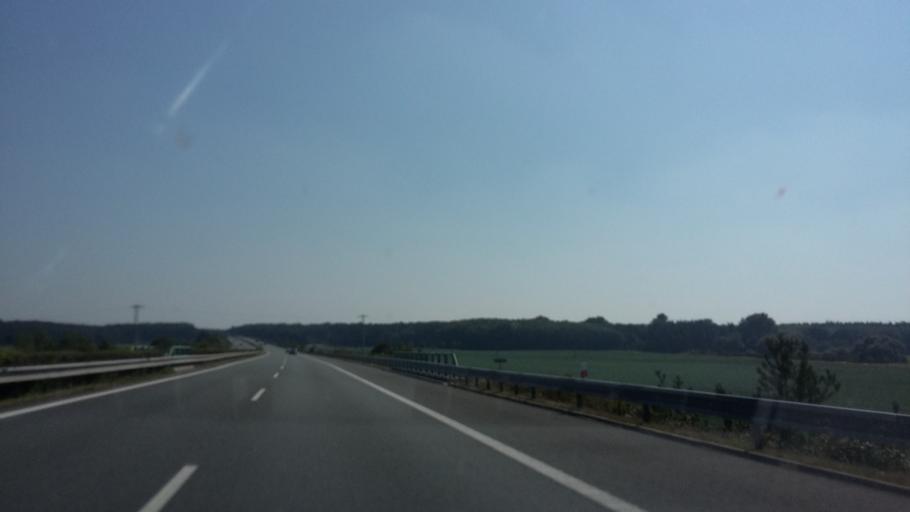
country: CZ
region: Central Bohemia
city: Velky Osek
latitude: 50.1168
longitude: 15.1976
